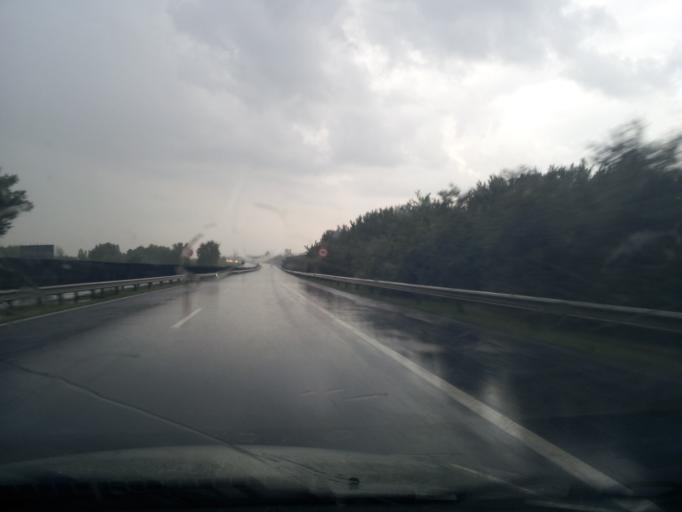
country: HU
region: Borsod-Abauj-Zemplen
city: Felsozsolca
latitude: 48.0854
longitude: 20.8513
